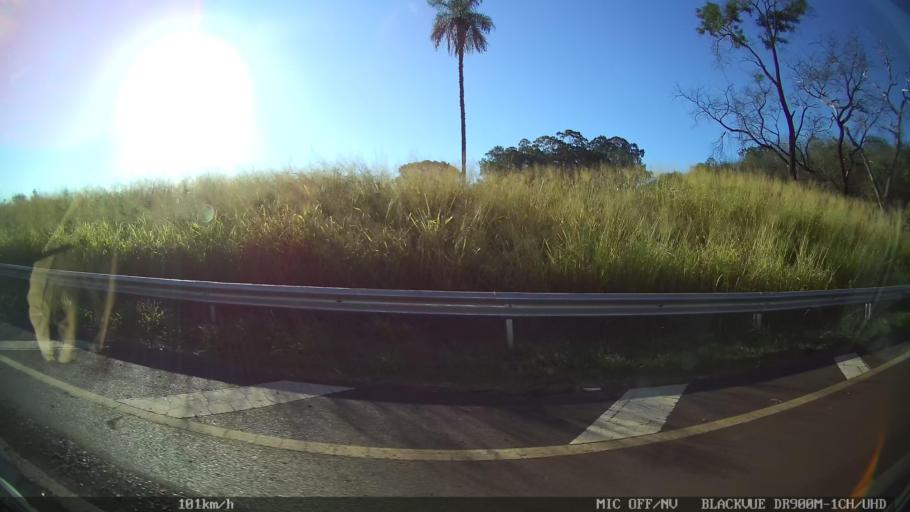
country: BR
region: Sao Paulo
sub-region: Guapiacu
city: Guapiacu
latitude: -20.7661
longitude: -49.1971
